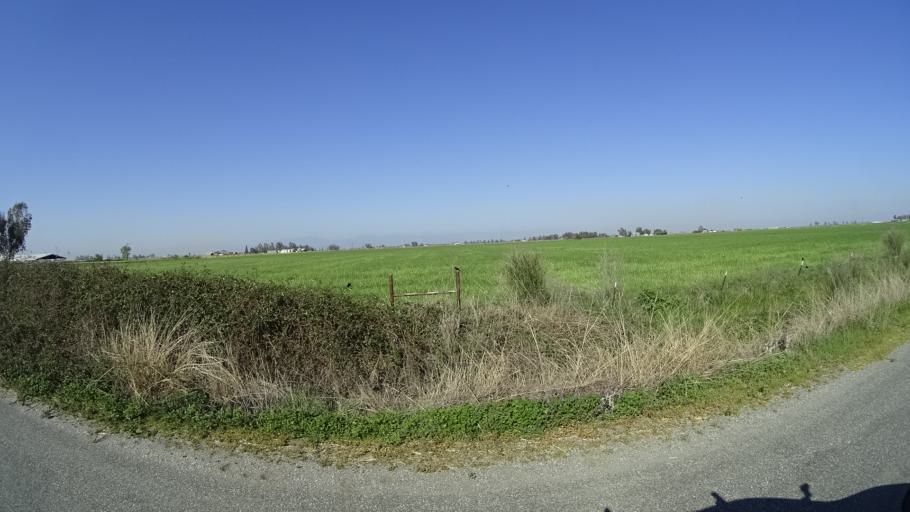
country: US
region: California
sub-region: Glenn County
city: Willows
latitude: 39.5772
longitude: -122.0839
